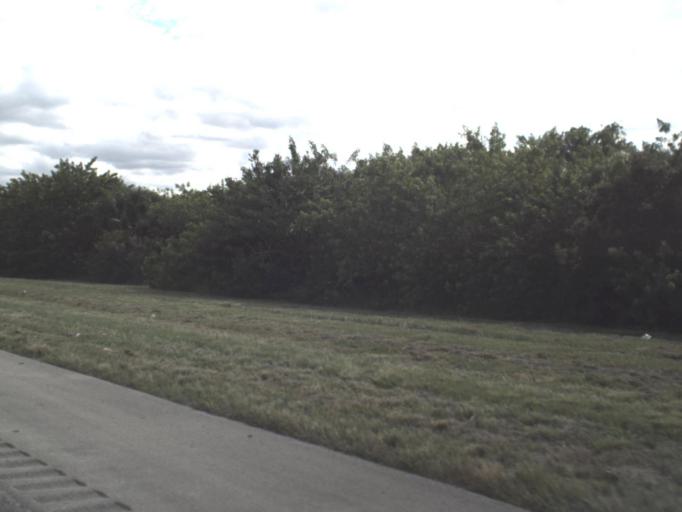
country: US
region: Florida
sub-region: Saint Lucie County
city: Lakewood Park
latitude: 27.4325
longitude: -80.4182
